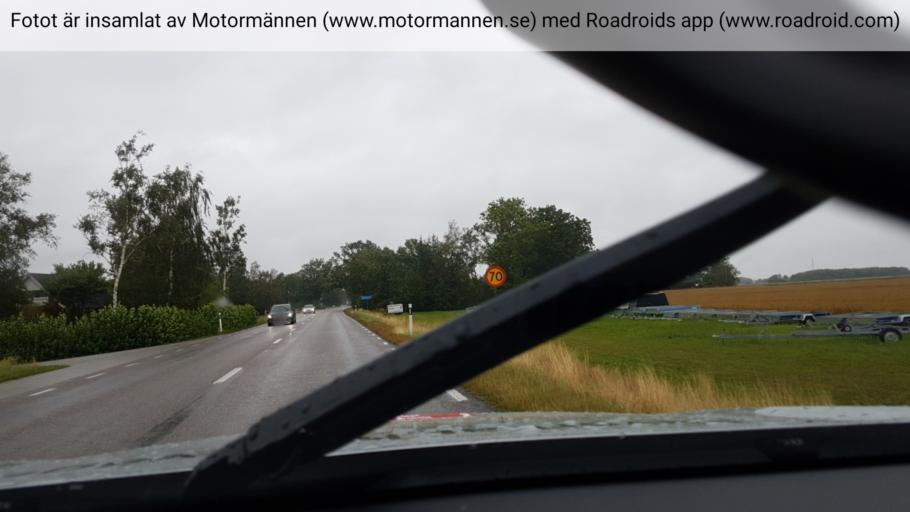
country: SE
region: Vaestra Goetaland
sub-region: Vanersborgs Kommun
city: Bralanda
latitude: 58.6280
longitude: 12.4152
